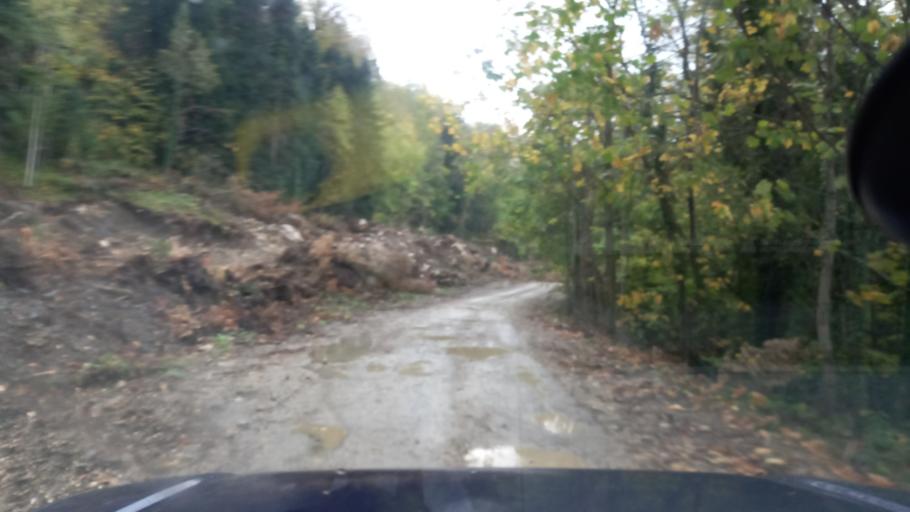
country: RU
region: Krasnodarskiy
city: Neftegorsk
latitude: 44.0464
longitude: 39.8332
